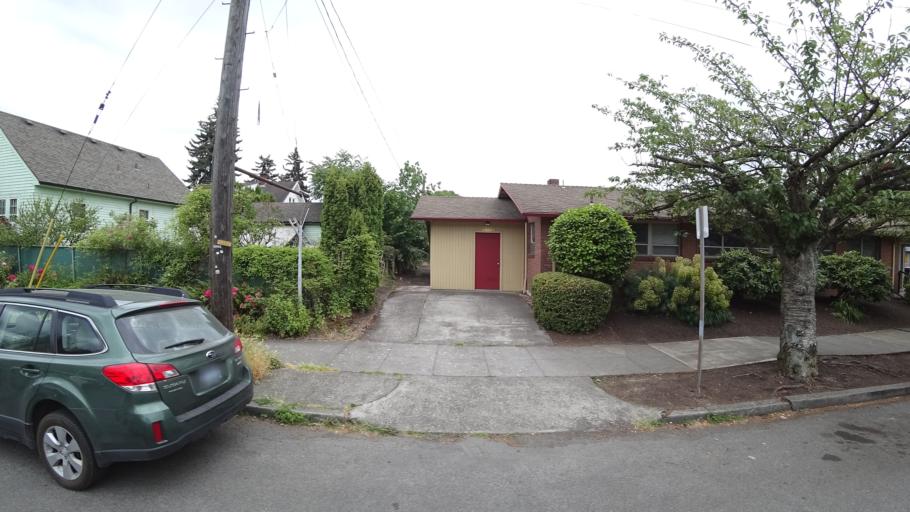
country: US
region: Oregon
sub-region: Multnomah County
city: Lents
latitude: 45.5203
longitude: -122.5811
